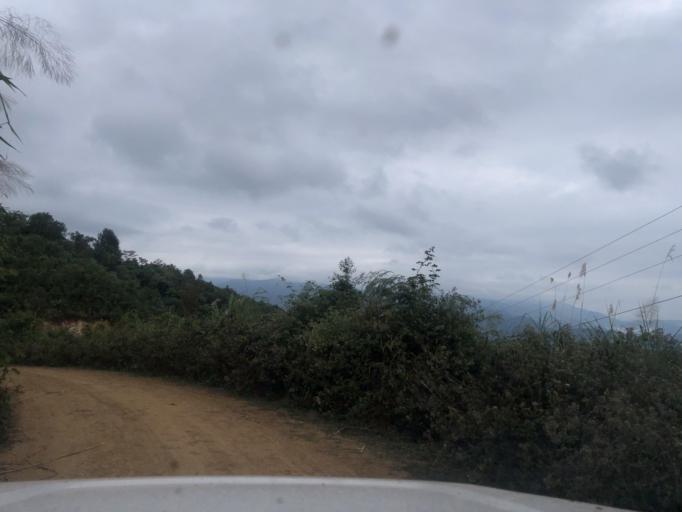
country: LA
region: Phongsali
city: Khoa
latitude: 21.2663
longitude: 102.5874
